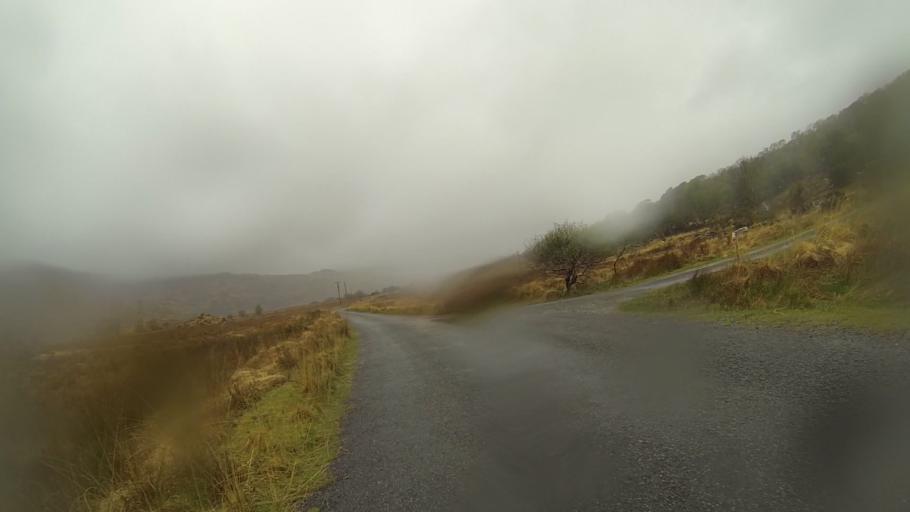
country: IE
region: Munster
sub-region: Ciarrai
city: Kenmare
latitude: 51.9510
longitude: -9.6483
